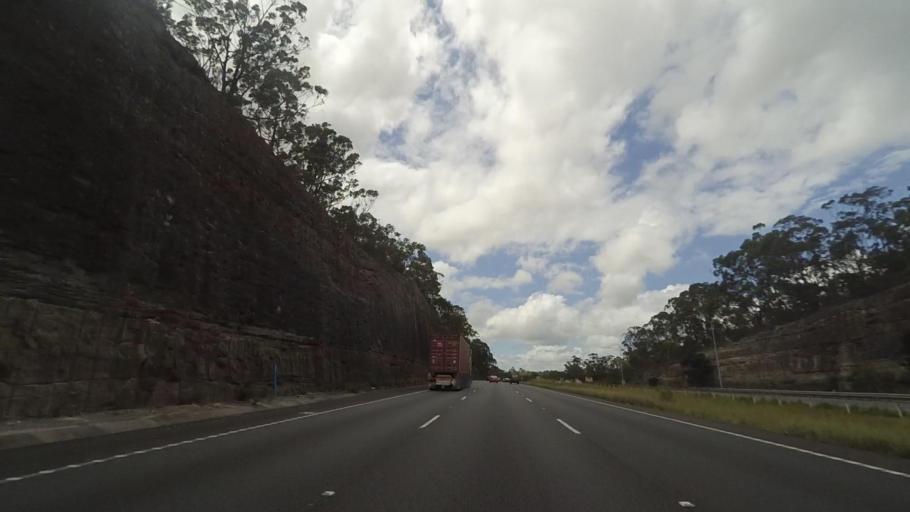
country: AU
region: New South Wales
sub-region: Gosford Shire
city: Point Clare
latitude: -33.4308
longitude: 151.2237
